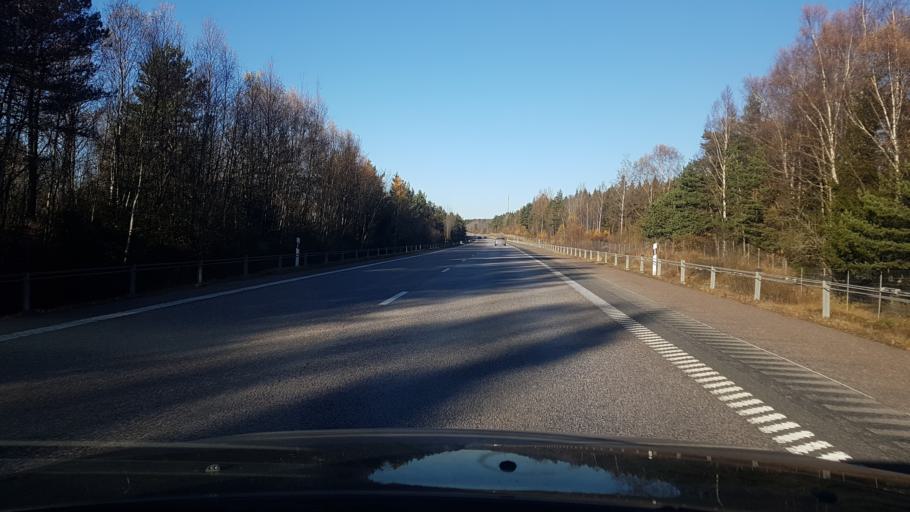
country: SE
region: Stockholm
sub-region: Sigtuna Kommun
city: Marsta
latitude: 59.6575
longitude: 17.8866
